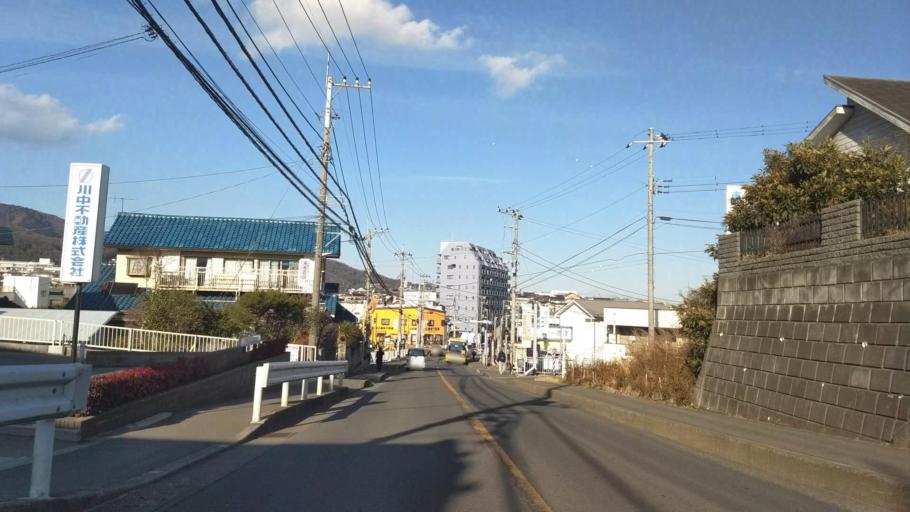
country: JP
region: Kanagawa
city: Isehara
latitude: 35.3708
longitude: 139.2735
